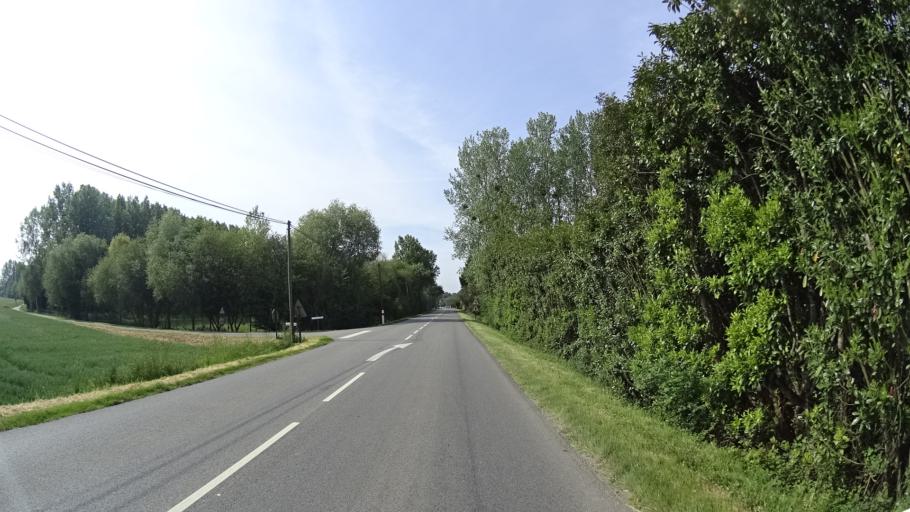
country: FR
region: Brittany
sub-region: Departement d'Ille-et-Vilaine
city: Chateaugiron
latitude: 48.0237
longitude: -1.5067
